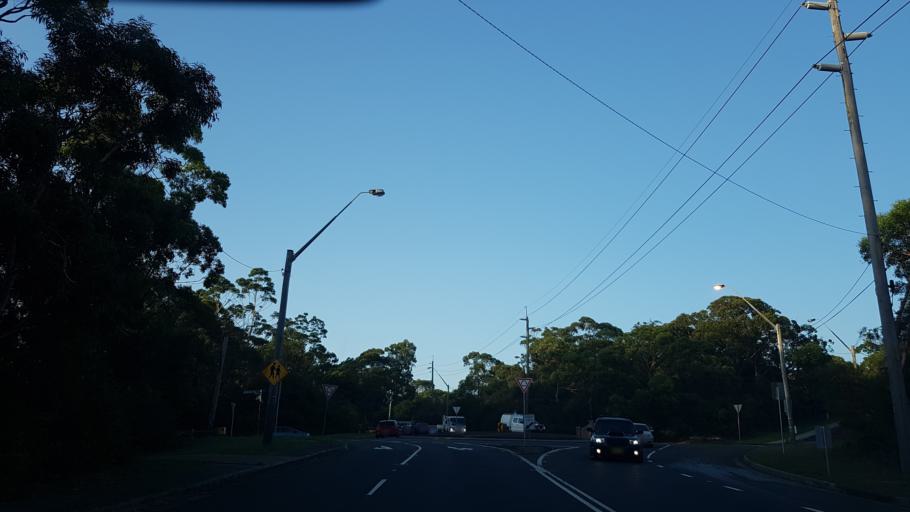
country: AU
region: New South Wales
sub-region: Warringah
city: Narraweena
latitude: -33.7473
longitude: 151.2630
